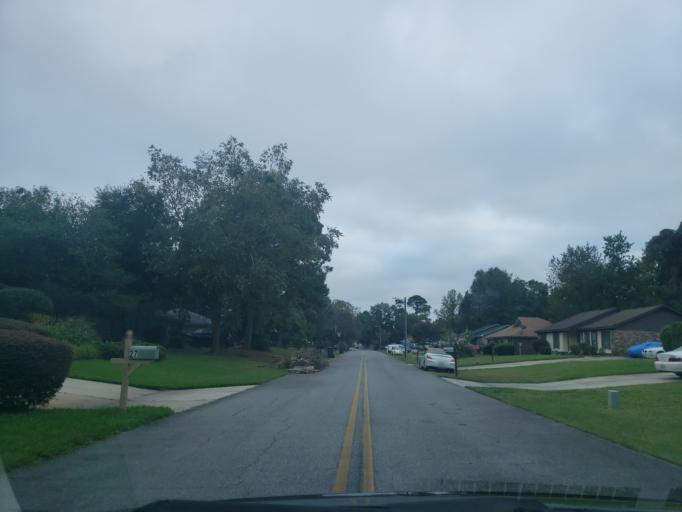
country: US
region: Georgia
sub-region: Chatham County
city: Montgomery
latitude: 31.9532
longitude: -81.1116
